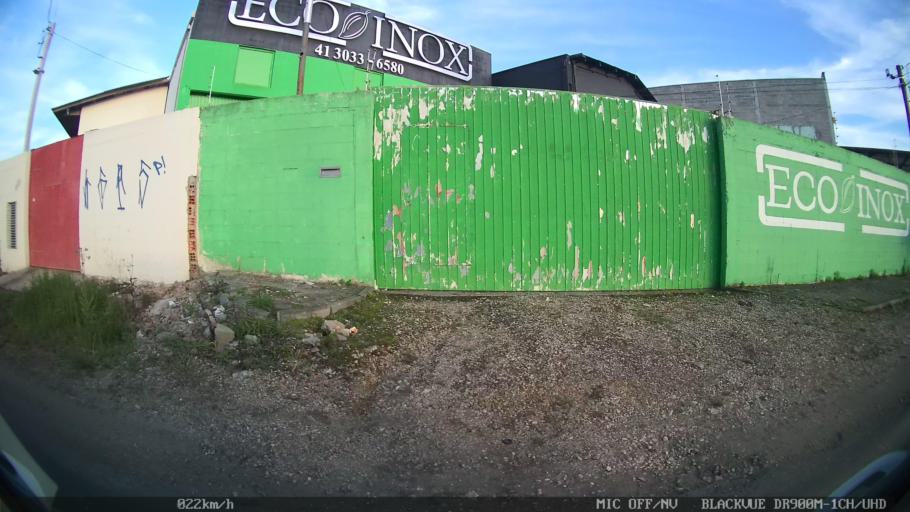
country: BR
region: Parana
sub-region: Pinhais
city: Pinhais
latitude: -25.4411
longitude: -49.1809
